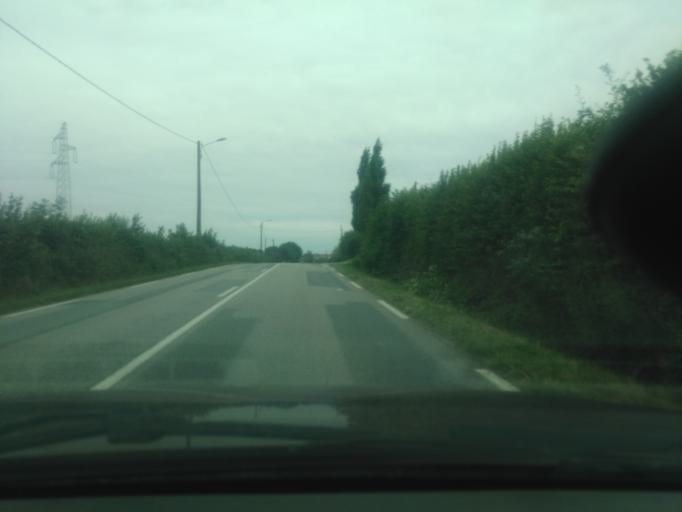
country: FR
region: Poitou-Charentes
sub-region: Departement des Deux-Sevres
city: Moncoutant
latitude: 46.6375
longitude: -0.5866
